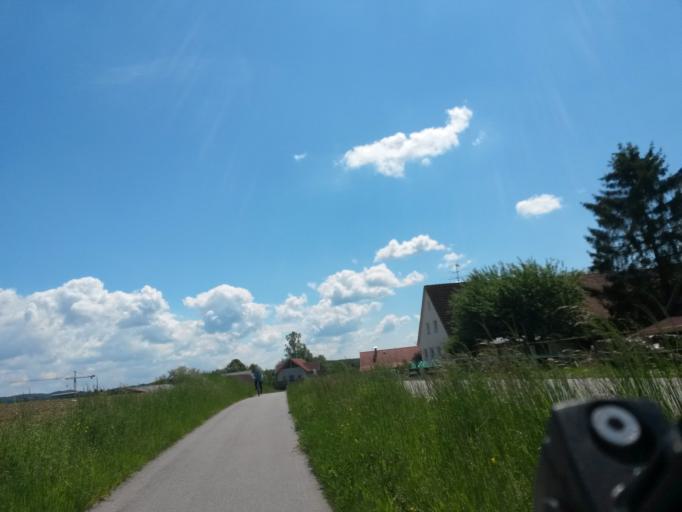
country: DE
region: Baden-Wuerttemberg
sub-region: Tuebingen Region
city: Bad Waldsee
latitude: 47.9385
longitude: 9.7490
